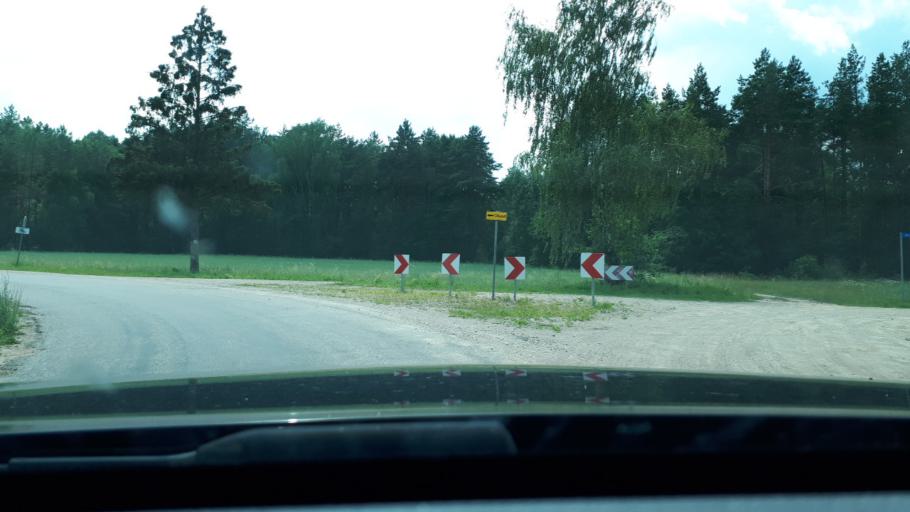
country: PL
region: Podlasie
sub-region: Powiat bialostocki
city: Lapy
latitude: 53.1040
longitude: 22.8651
